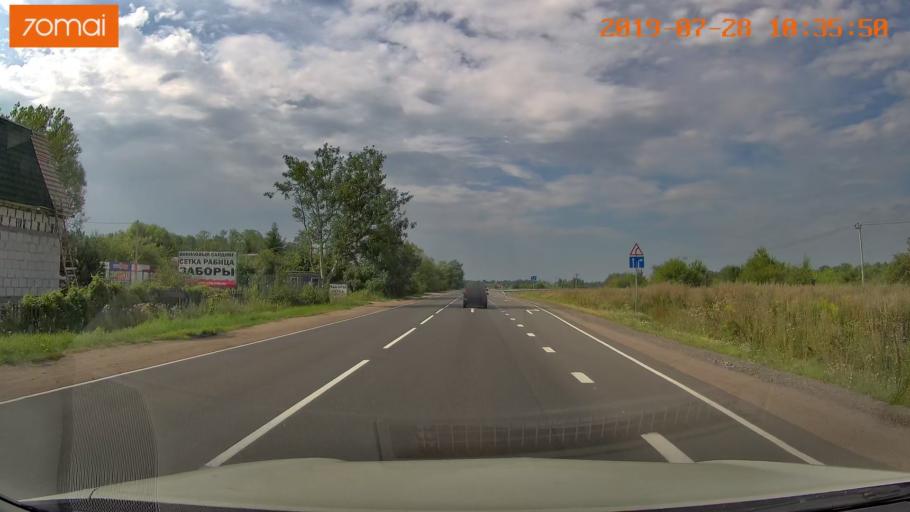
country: RU
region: Kaliningrad
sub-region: Gorod Kaliningrad
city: Kaliningrad
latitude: 54.7430
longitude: 20.4277
